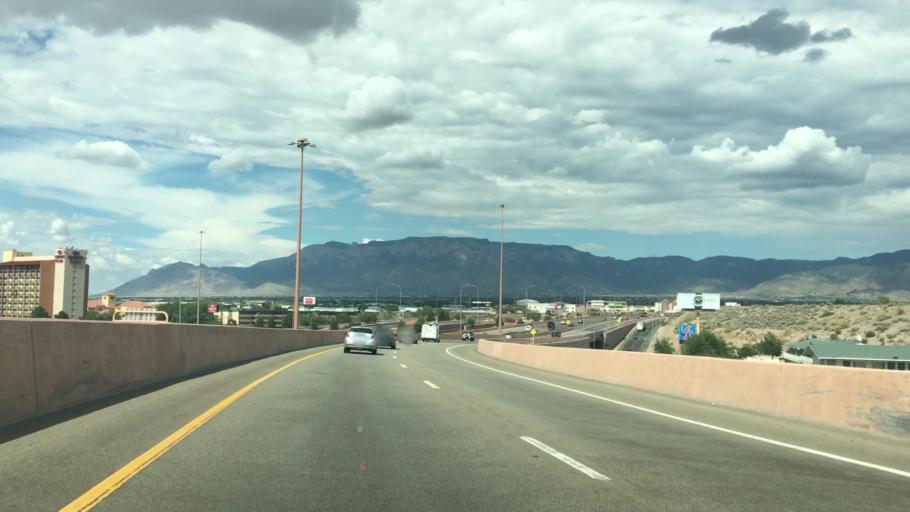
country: US
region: New Mexico
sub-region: Bernalillo County
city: Albuquerque
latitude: 35.1045
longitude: -106.6268
